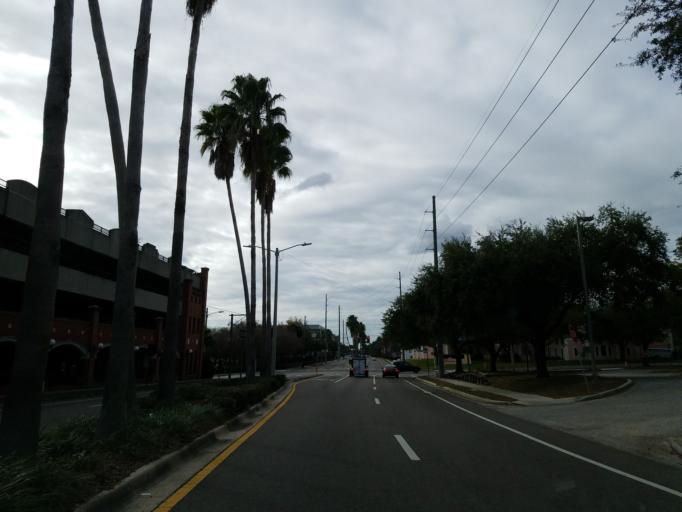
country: US
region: Florida
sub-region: Hillsborough County
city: Tampa
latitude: 27.9624
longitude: -82.4458
